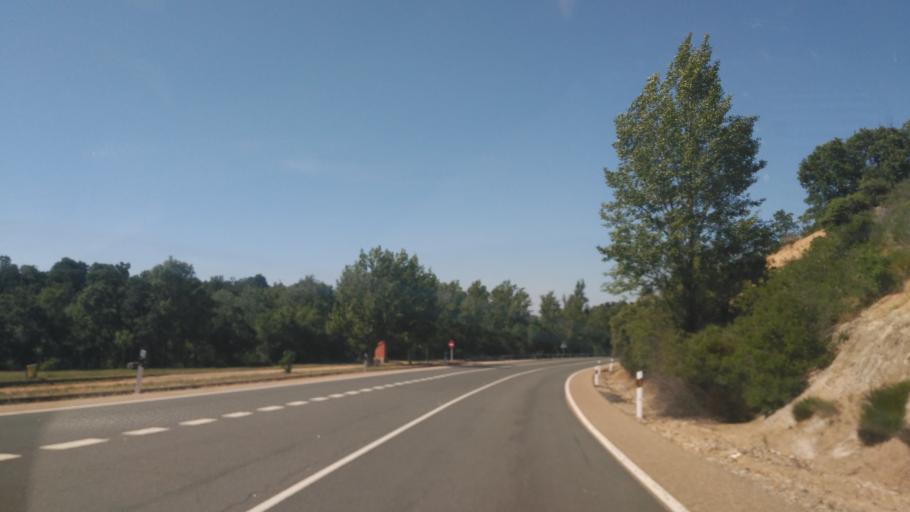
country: ES
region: Castille and Leon
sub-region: Provincia de Zamora
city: Corrales
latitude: 41.3040
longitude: -5.7275
